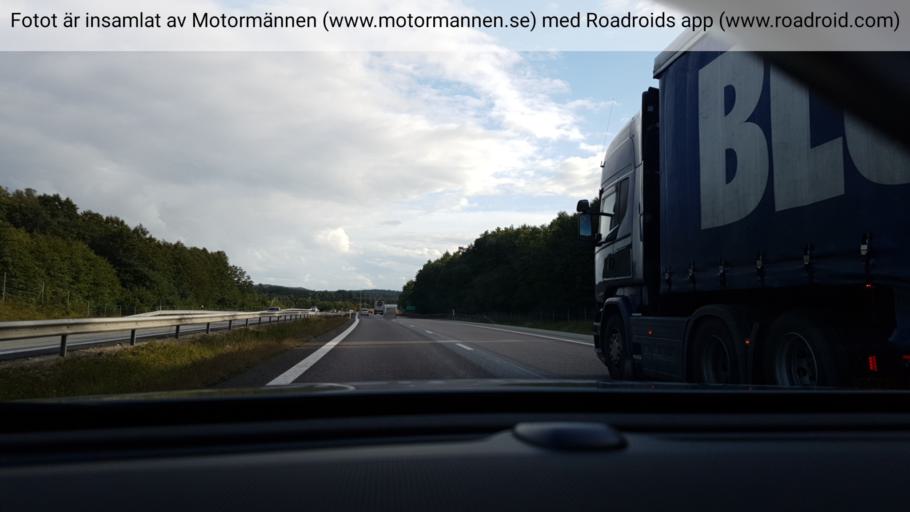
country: SE
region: Vaestra Goetaland
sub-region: Stenungsunds Kommun
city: Stora Hoga
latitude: 58.0356
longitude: 11.8457
